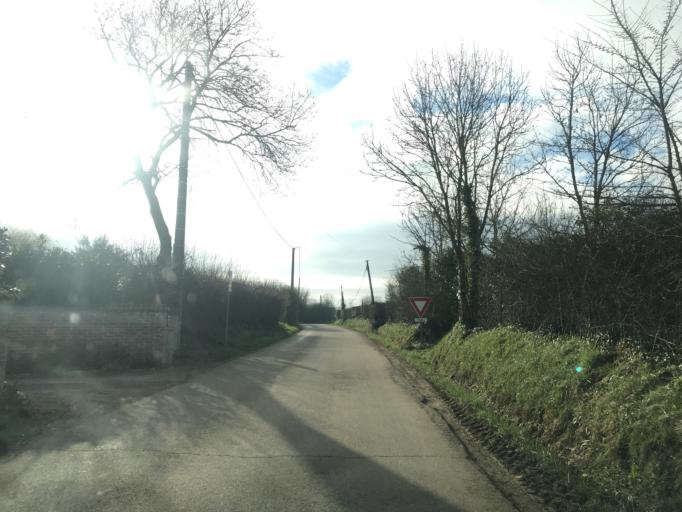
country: FR
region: Lower Normandy
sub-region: Departement du Calvados
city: Dozule
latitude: 49.2192
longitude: -0.1013
